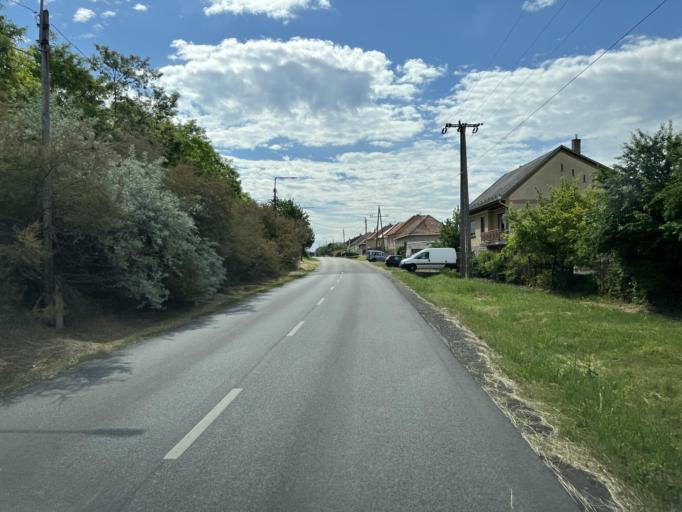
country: HU
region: Pest
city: Zsambok
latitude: 47.5488
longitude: 19.6002
